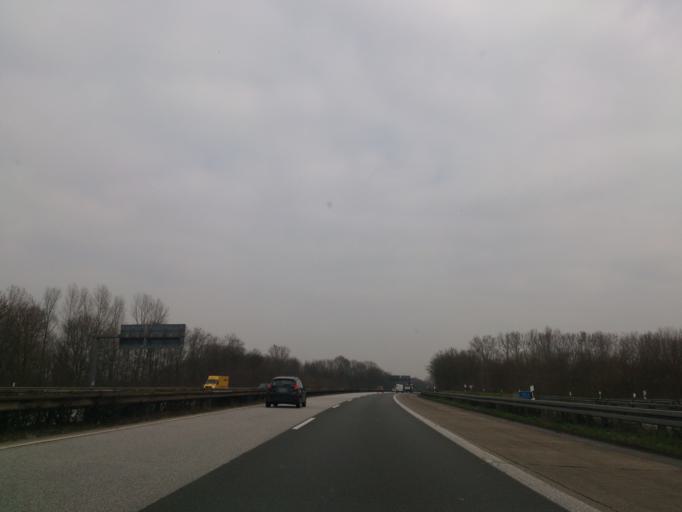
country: DE
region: North Rhine-Westphalia
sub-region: Regierungsbezirk Dusseldorf
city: Korschenbroich
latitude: 51.2425
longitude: 6.4896
